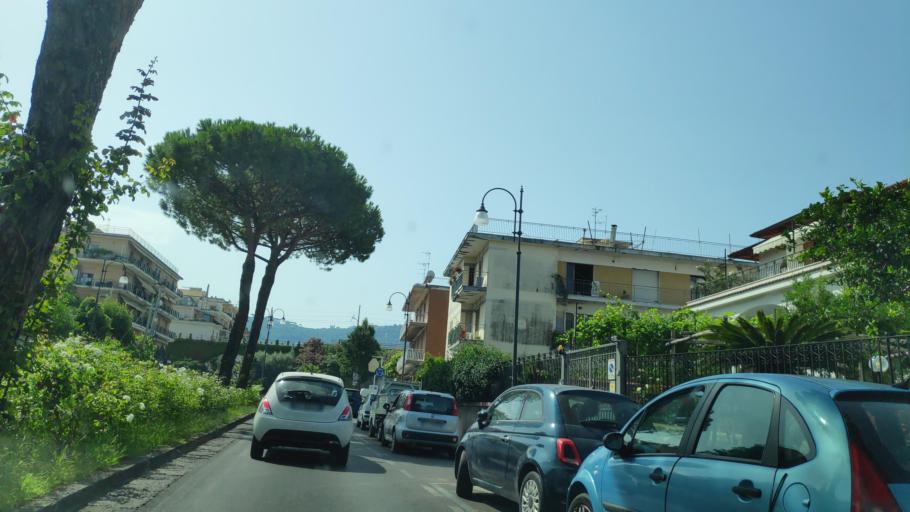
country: IT
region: Campania
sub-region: Provincia di Napoli
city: Sant'Agnello
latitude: 40.6322
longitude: 14.3978
